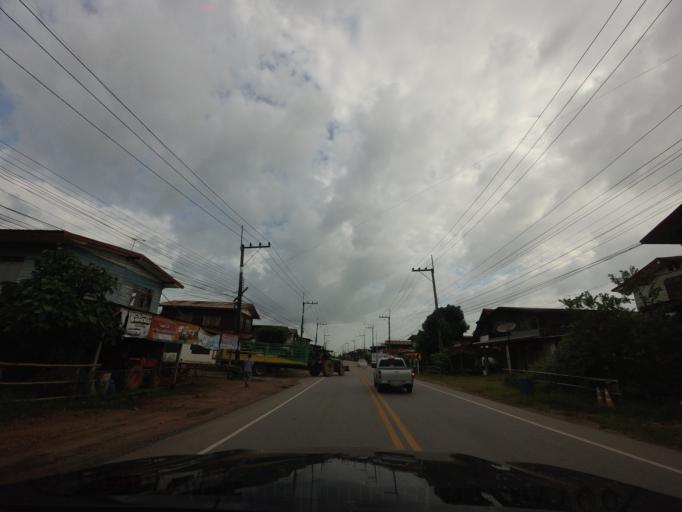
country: TH
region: Changwat Udon Thani
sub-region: Amphoe Ban Phue
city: Ban Phue
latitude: 17.7445
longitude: 102.3993
